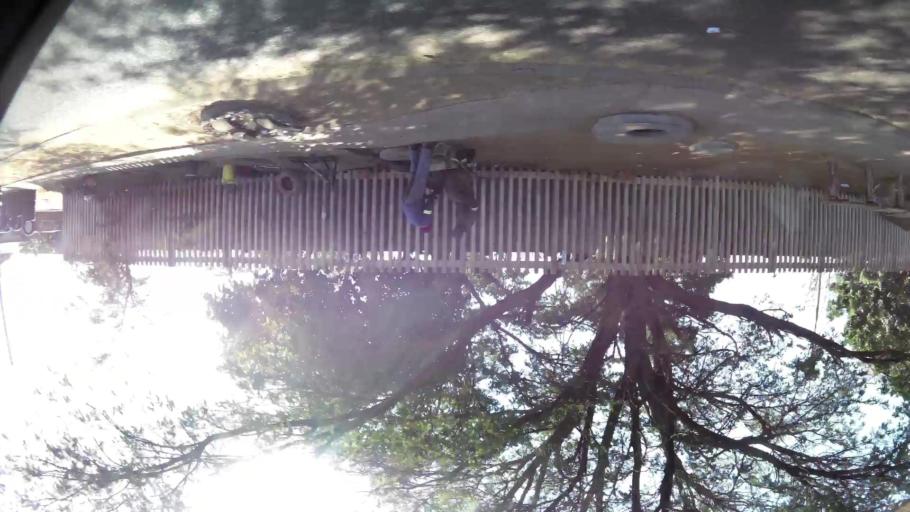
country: ZA
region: Gauteng
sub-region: City of Tshwane Metropolitan Municipality
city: Mabopane
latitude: -25.5367
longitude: 28.0999
